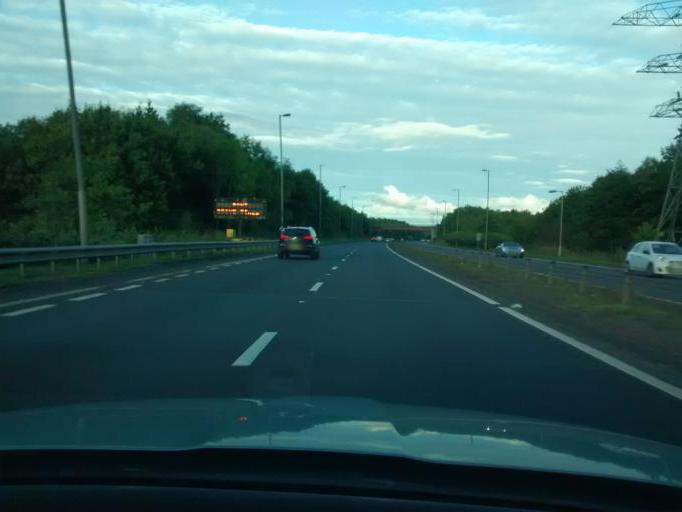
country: GB
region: Scotland
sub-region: Renfrewshire
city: Johnstone
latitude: 55.8418
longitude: -4.5091
